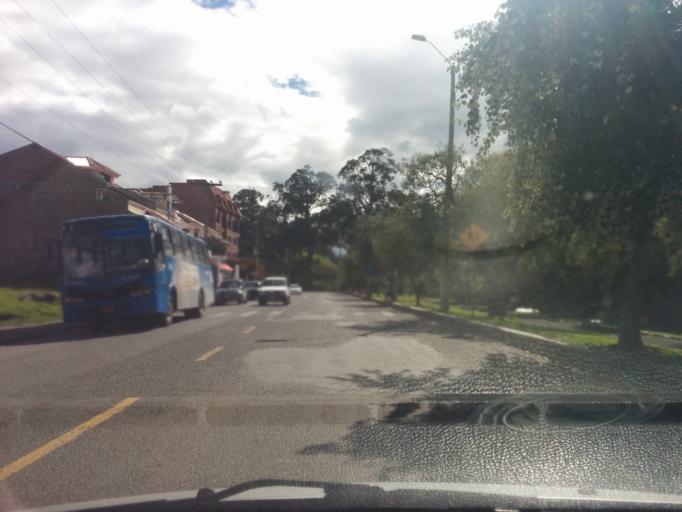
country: EC
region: Azuay
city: Cuenca
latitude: -2.9160
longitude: -78.9965
